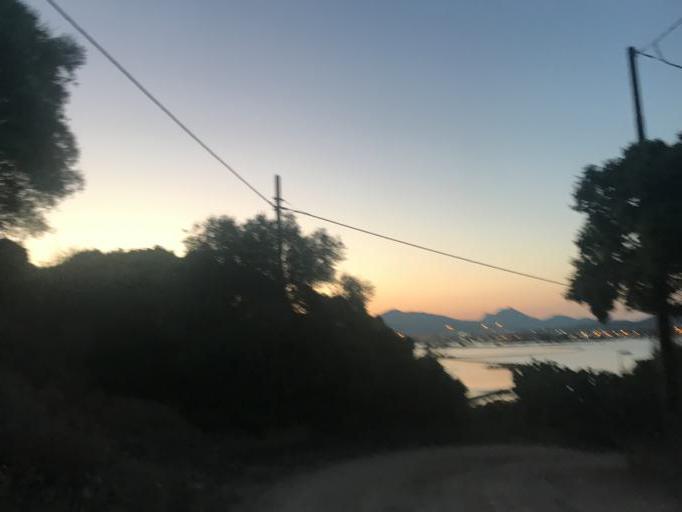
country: IT
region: Sardinia
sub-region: Provincia di Olbia-Tempio
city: Olbia
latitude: 40.9122
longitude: 9.5148
